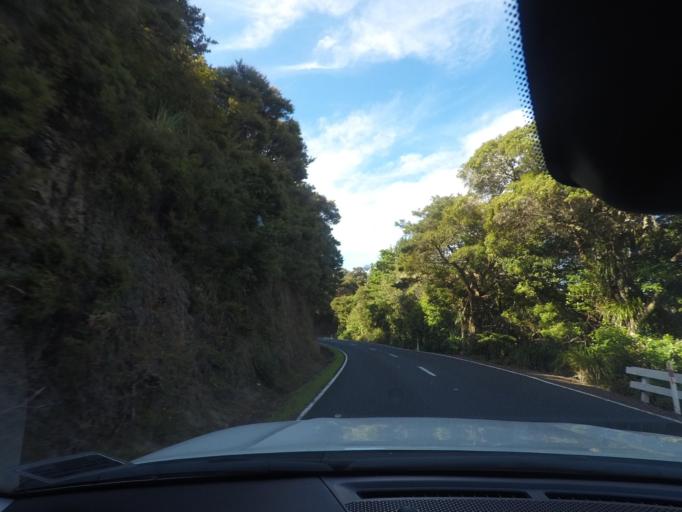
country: NZ
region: Northland
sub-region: Whangarei
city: Ngunguru
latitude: -35.6677
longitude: 174.4699
